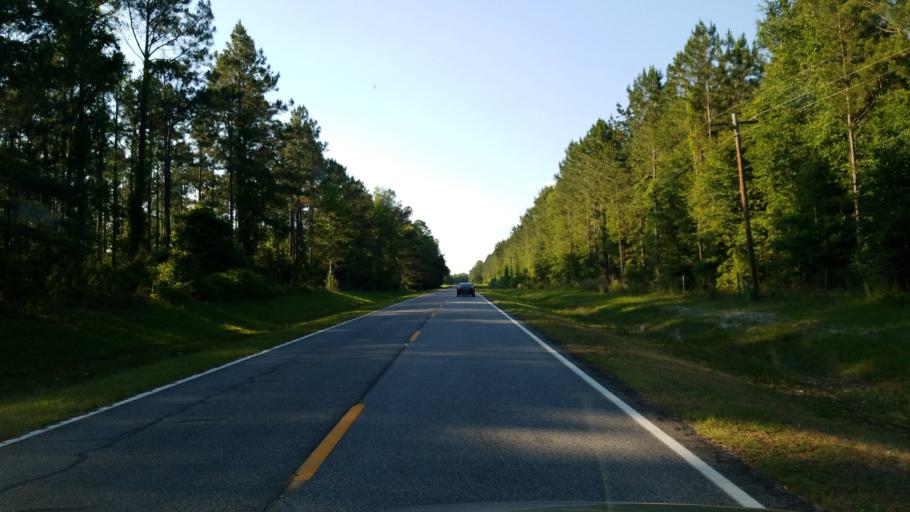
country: US
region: Georgia
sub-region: Lanier County
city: Lakeland
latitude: 30.9612
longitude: -83.0820
